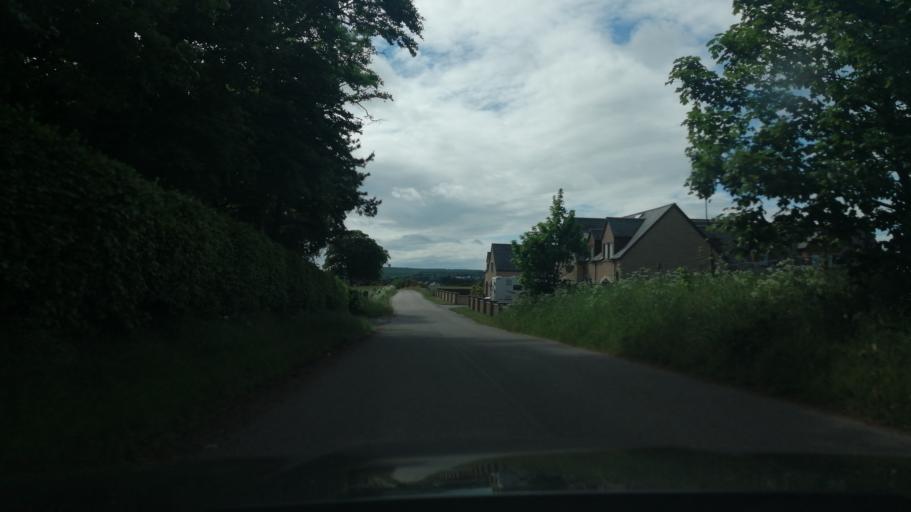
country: GB
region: Scotland
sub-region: Moray
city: Elgin
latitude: 57.6542
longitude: -3.2852
